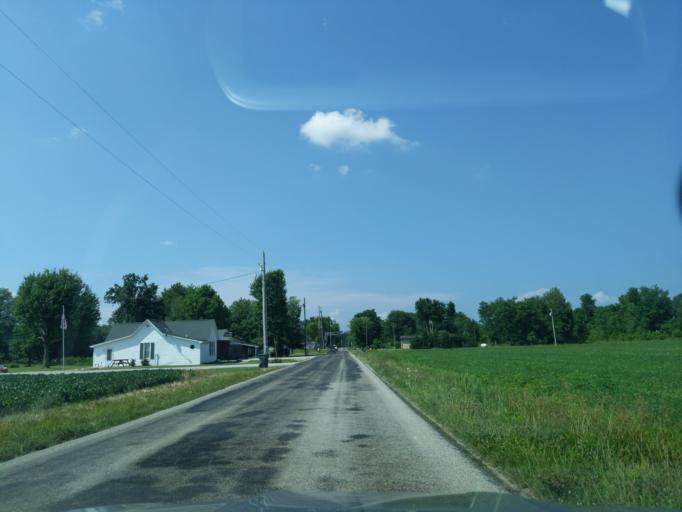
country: US
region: Indiana
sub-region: Ripley County
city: Osgood
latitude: 39.0881
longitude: -85.3469
